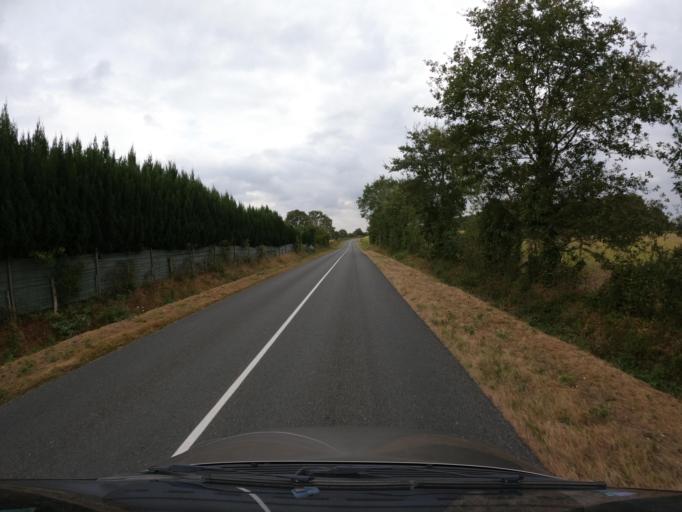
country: FR
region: Pays de la Loire
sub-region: Departement de Maine-et-Loire
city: Le Longeron
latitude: 47.0368
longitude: -1.0384
